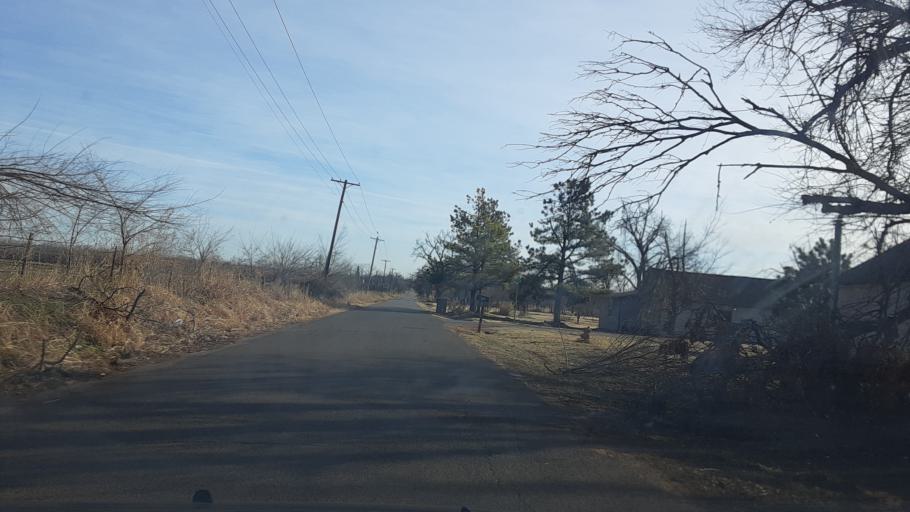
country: US
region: Oklahoma
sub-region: Logan County
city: Guthrie
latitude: 35.8853
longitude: -97.4384
